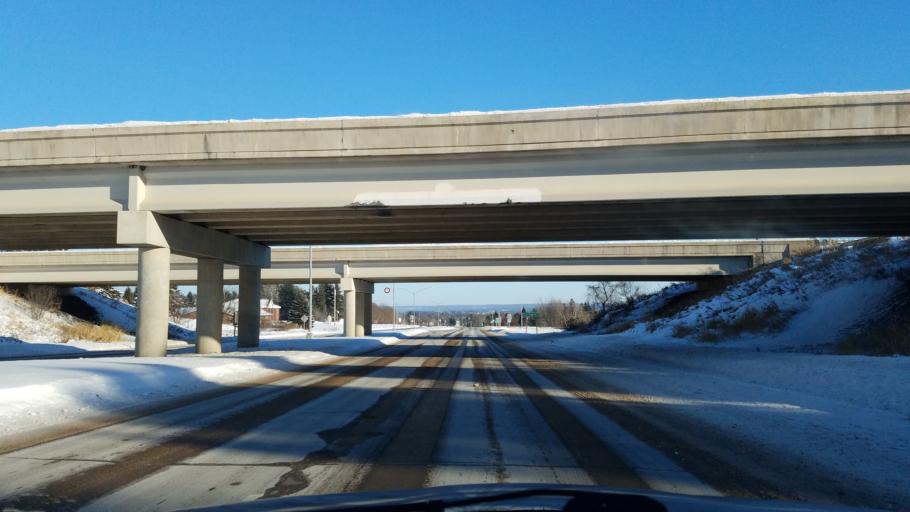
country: US
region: Wisconsin
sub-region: Barron County
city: Rice Lake
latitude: 45.5093
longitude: -91.7626
